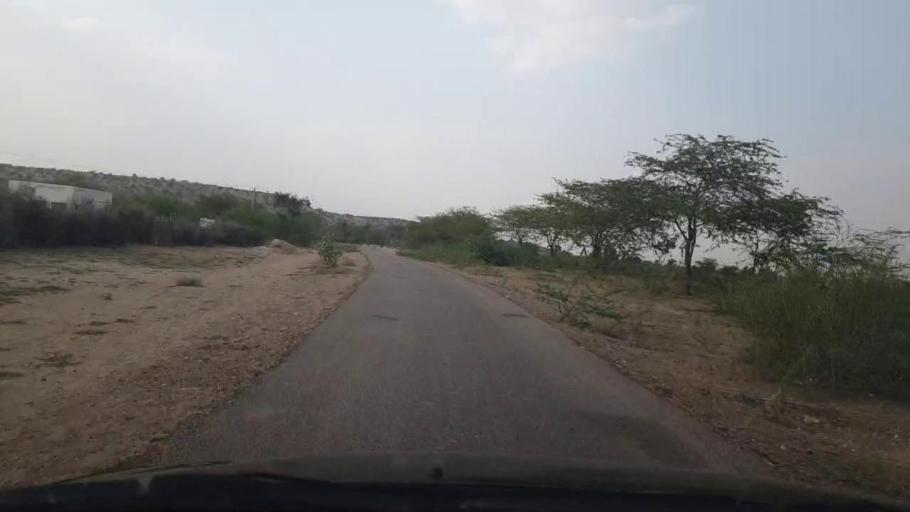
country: PK
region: Sindh
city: Islamkot
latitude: 25.0292
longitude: 70.5554
